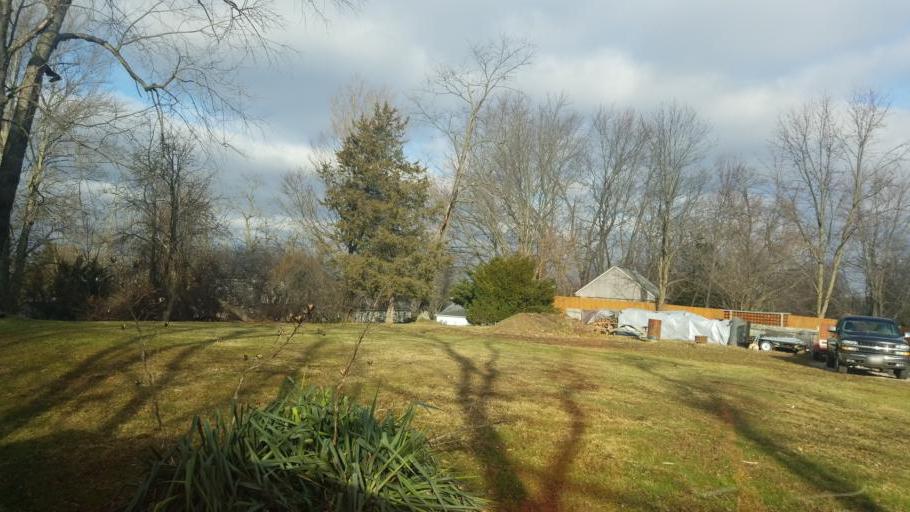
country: US
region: Ohio
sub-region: Richland County
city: Ontario
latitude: 40.7576
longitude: -82.6018
